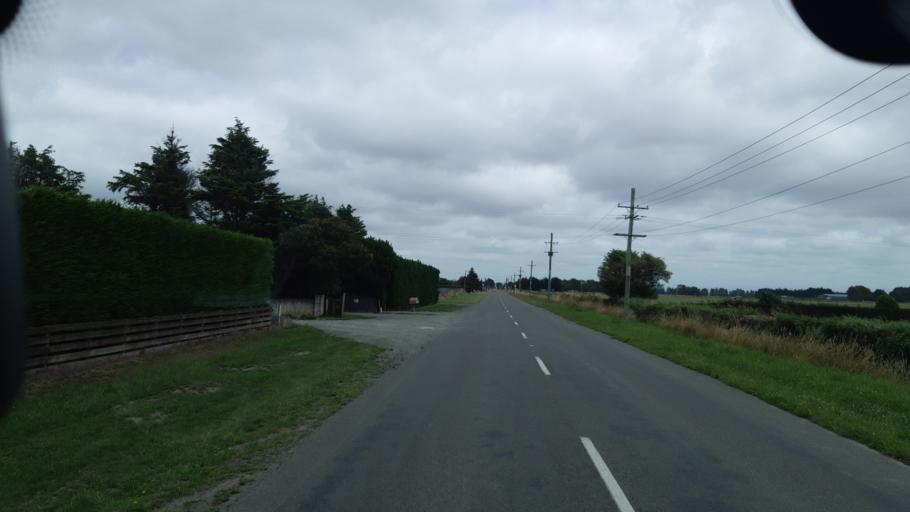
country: NZ
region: Canterbury
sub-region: Selwyn District
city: Prebbleton
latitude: -43.5070
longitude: 172.5206
